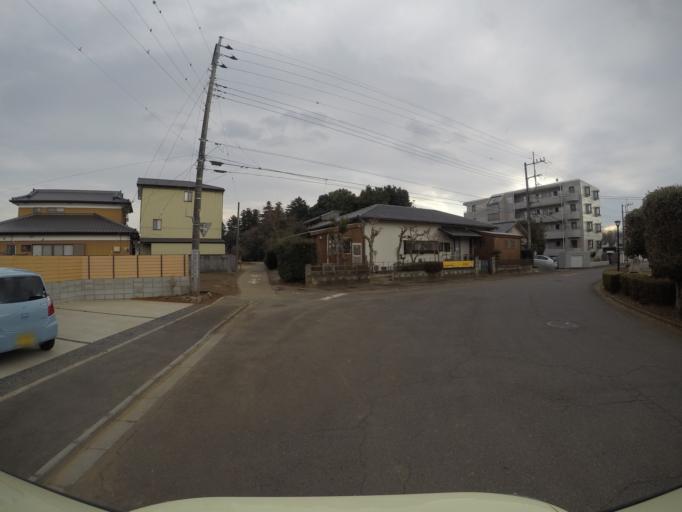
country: JP
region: Ibaraki
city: Tsukuba
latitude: 36.1263
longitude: 140.0960
